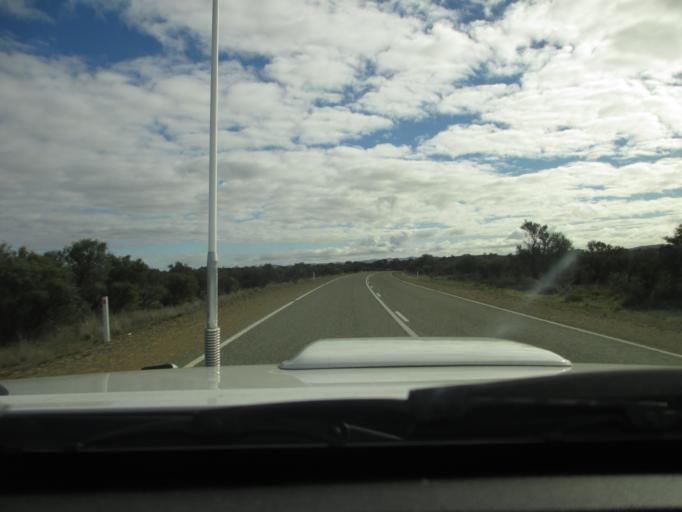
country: AU
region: South Australia
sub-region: Flinders Ranges
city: Quorn
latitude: -32.3791
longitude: 138.5002
